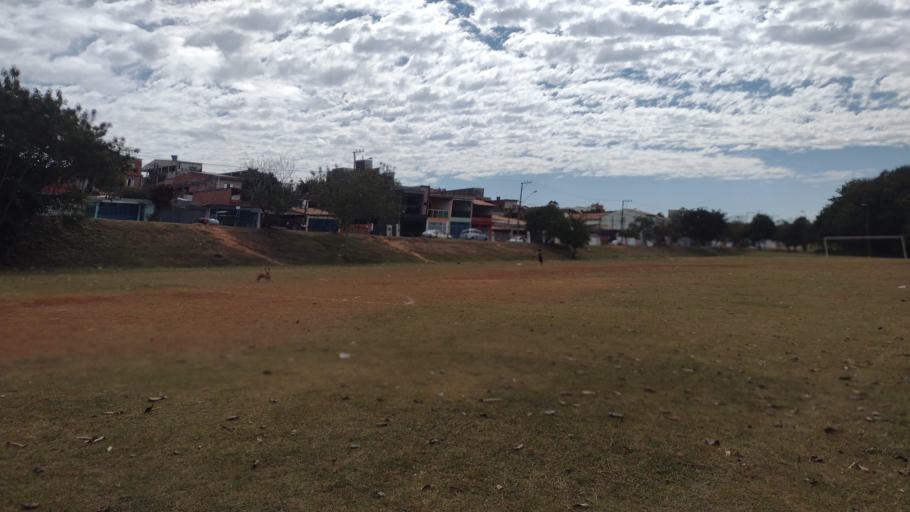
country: BR
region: Sao Paulo
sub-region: Sorocaba
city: Sorocaba
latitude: -23.4283
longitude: -47.4543
